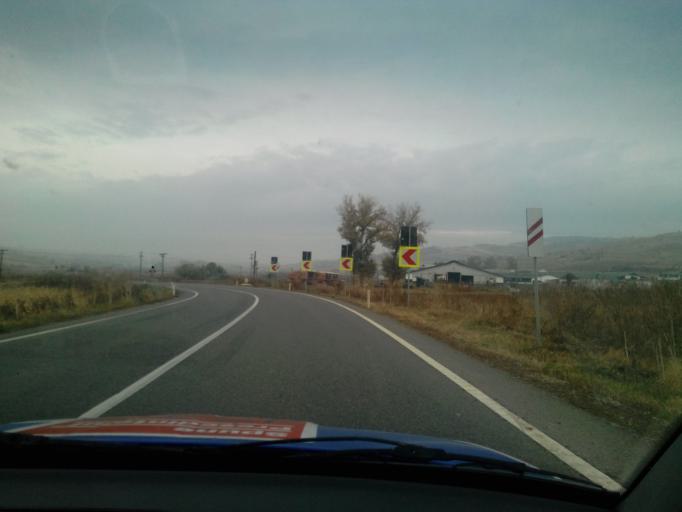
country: RO
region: Vaslui
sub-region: Comuna Albesti
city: Corni-Albesti
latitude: 46.5497
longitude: 27.8544
